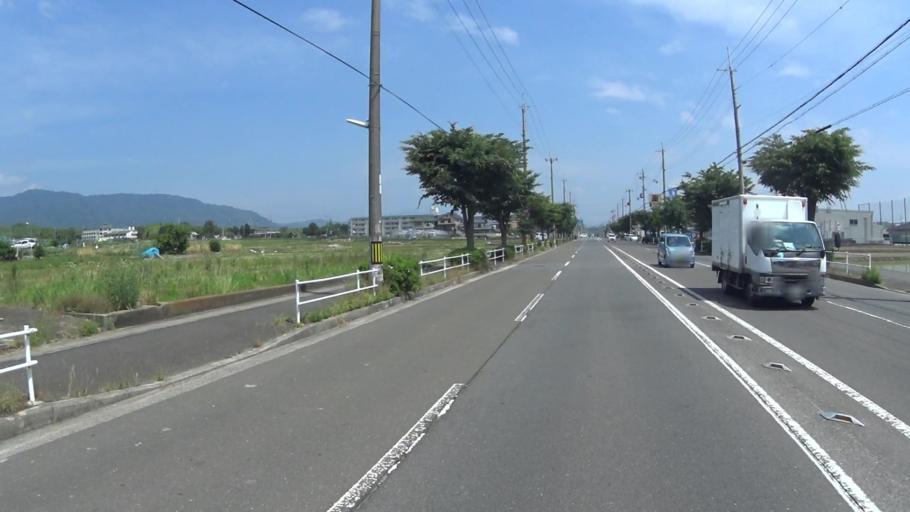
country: JP
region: Kyoto
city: Muko
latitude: 34.9367
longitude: 135.6858
